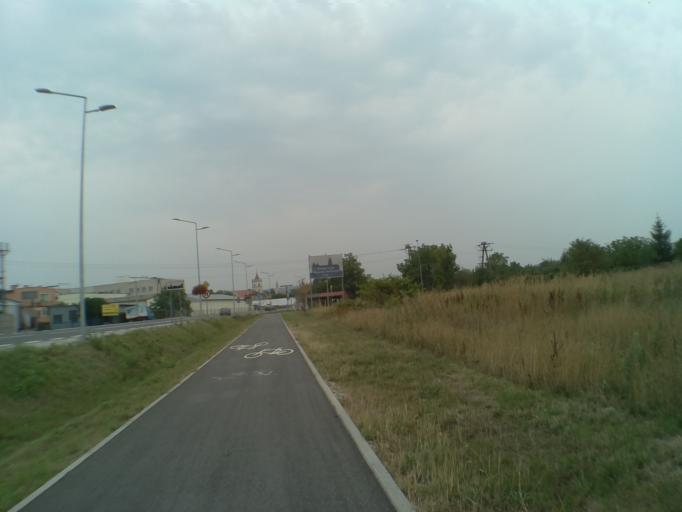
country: PL
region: Lower Silesian Voivodeship
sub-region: Powiat swidnicki
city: Swiebodzice
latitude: 50.8699
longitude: 16.3268
